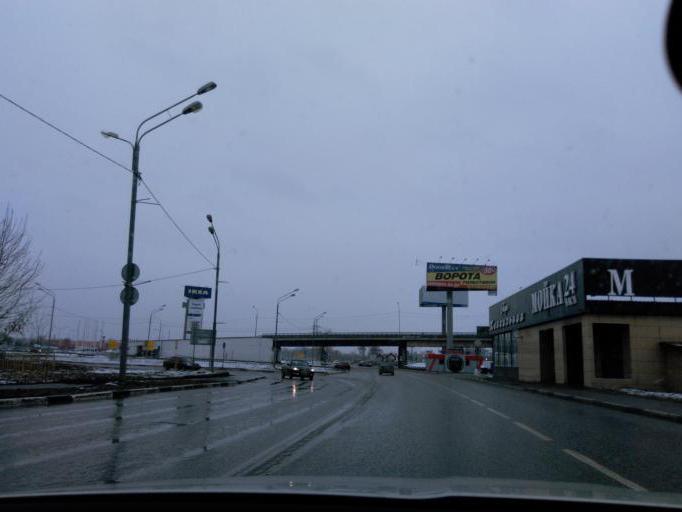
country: RU
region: Moscow
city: Khimki
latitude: 55.9101
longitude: 37.4062
